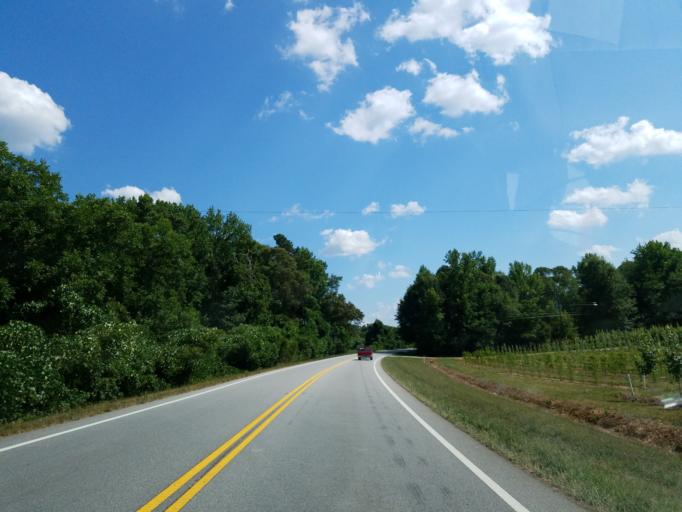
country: US
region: Georgia
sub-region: Lamar County
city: Barnesville
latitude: 33.0029
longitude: -84.1201
